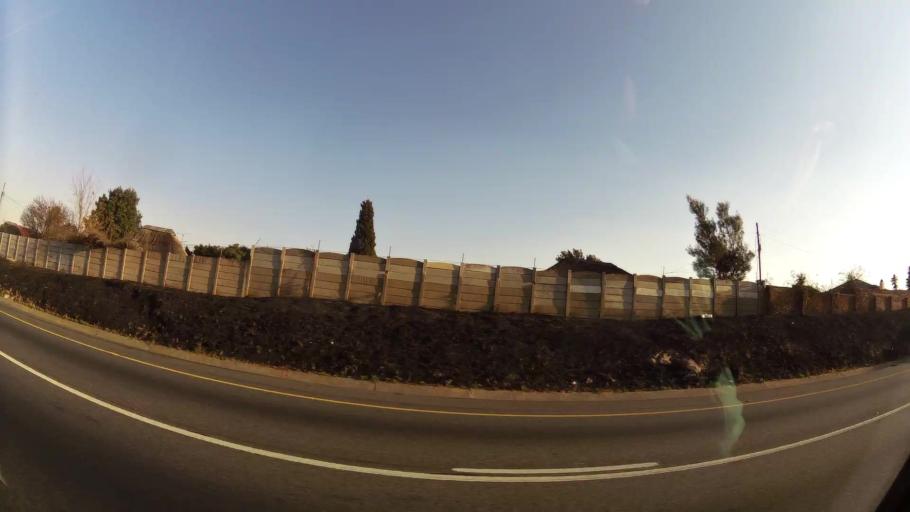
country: ZA
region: Gauteng
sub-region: City of Johannesburg Metropolitan Municipality
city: Johannesburg
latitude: -26.2689
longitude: 28.0364
